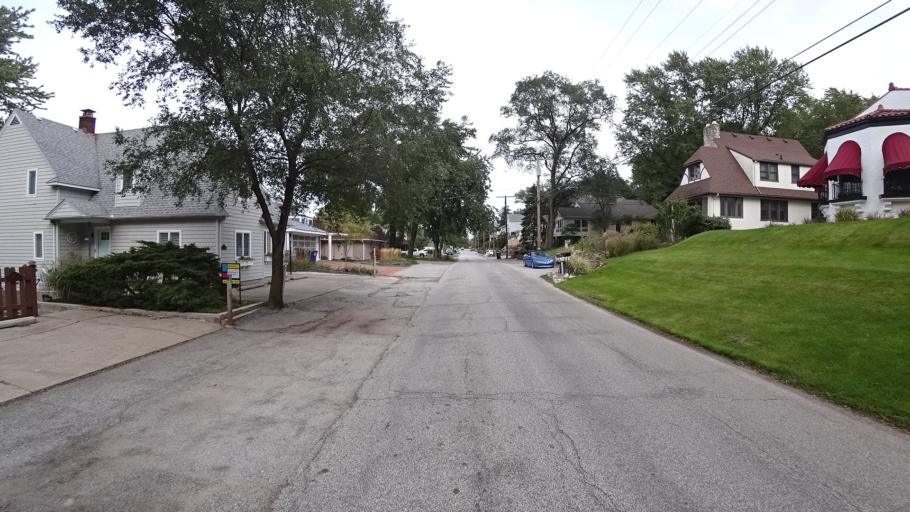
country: US
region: Indiana
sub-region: LaPorte County
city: Long Beach
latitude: 41.7424
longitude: -86.8635
